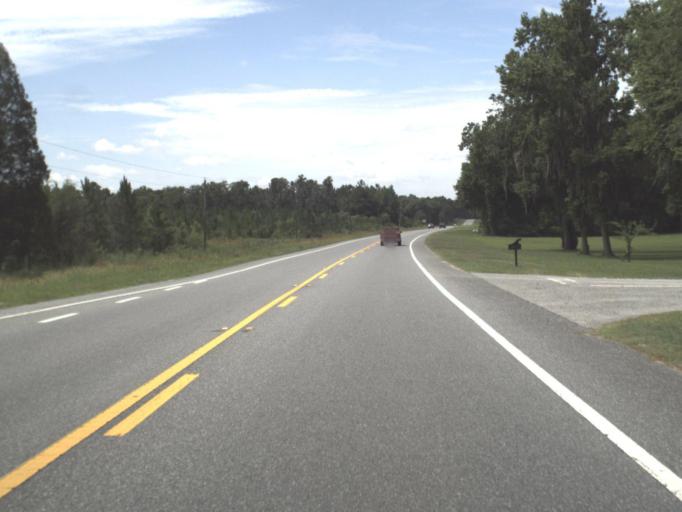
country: US
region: Florida
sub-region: Suwannee County
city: Live Oak
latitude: 30.3640
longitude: -82.9420
